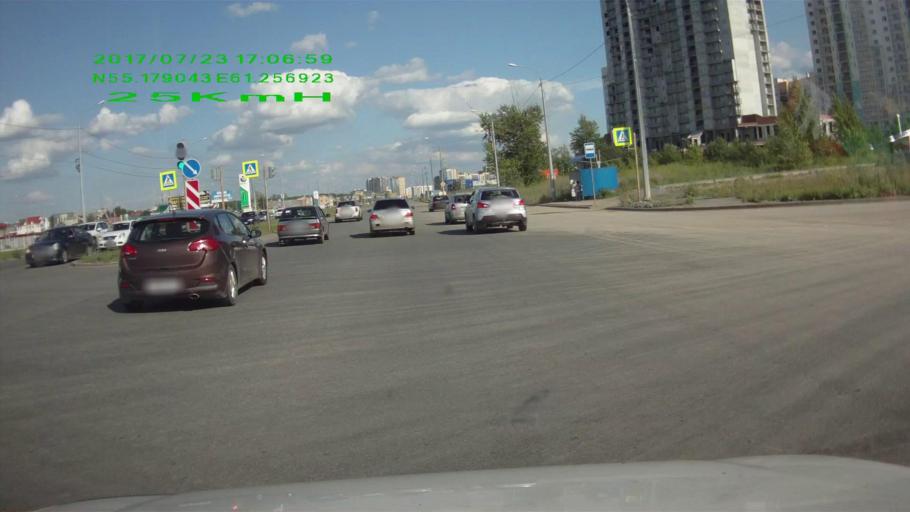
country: RU
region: Chelyabinsk
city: Roshchino
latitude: 55.1788
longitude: 61.2578
